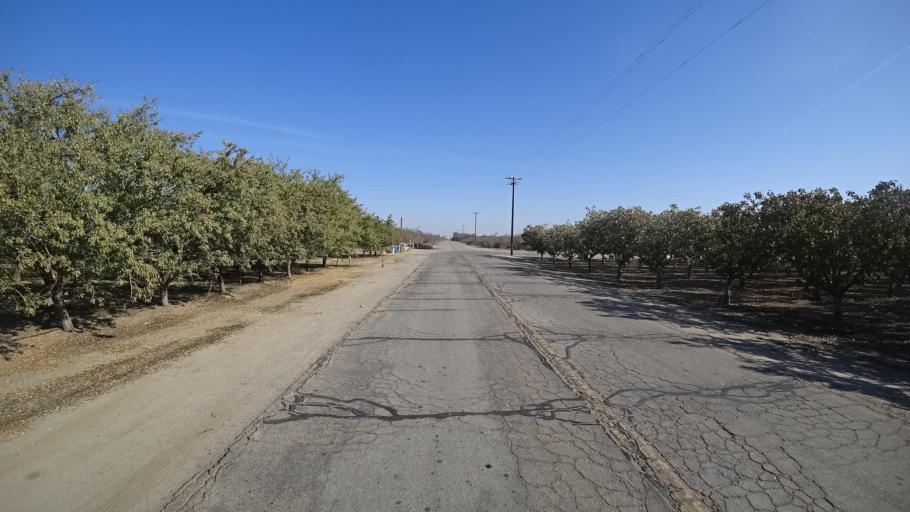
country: US
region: California
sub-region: Kern County
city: Wasco
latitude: 35.6669
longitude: -119.3492
